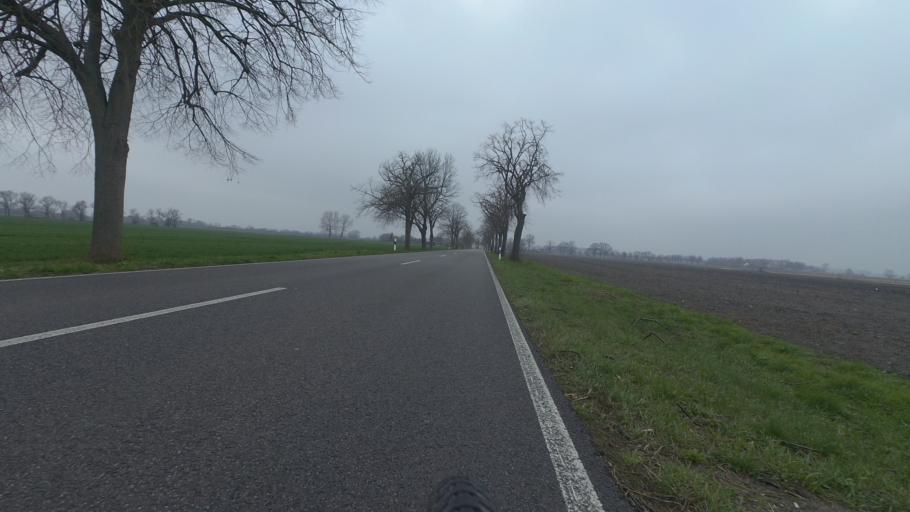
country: DE
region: Brandenburg
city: Nauen
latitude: 52.6278
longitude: 12.8571
